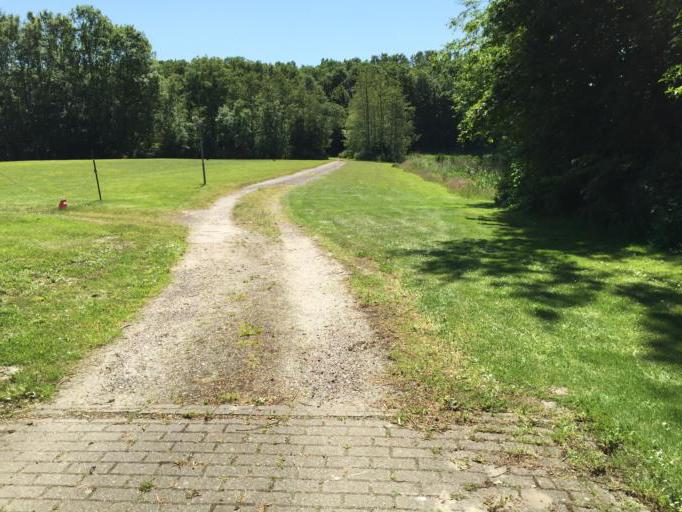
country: NL
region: Groningen
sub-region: Gemeente De Marne
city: Ulrum
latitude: 53.3415
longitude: 6.2968
